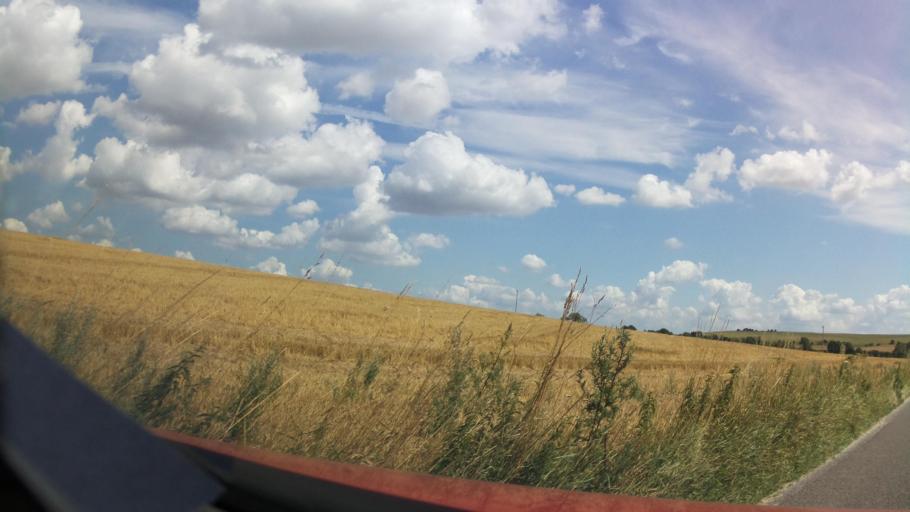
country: GB
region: England
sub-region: West Berkshire
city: Lambourn
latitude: 51.5242
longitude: -1.5790
